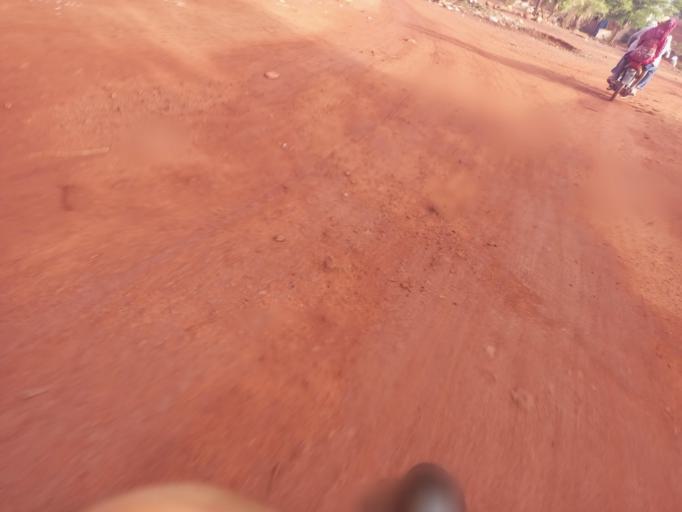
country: ML
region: Bamako
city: Bamako
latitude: 12.5218
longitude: -7.9941
